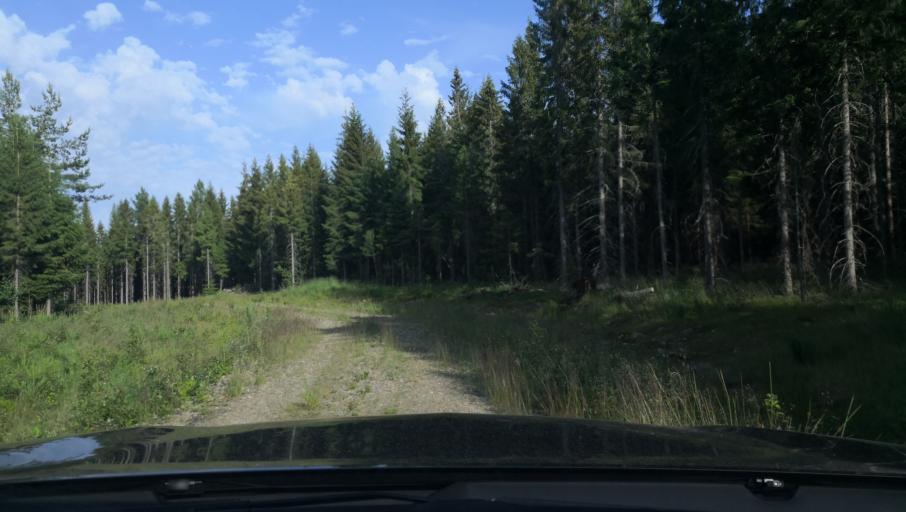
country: SE
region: Dalarna
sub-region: Smedjebackens Kommun
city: Smedjebacken
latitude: 59.9741
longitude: 15.3837
